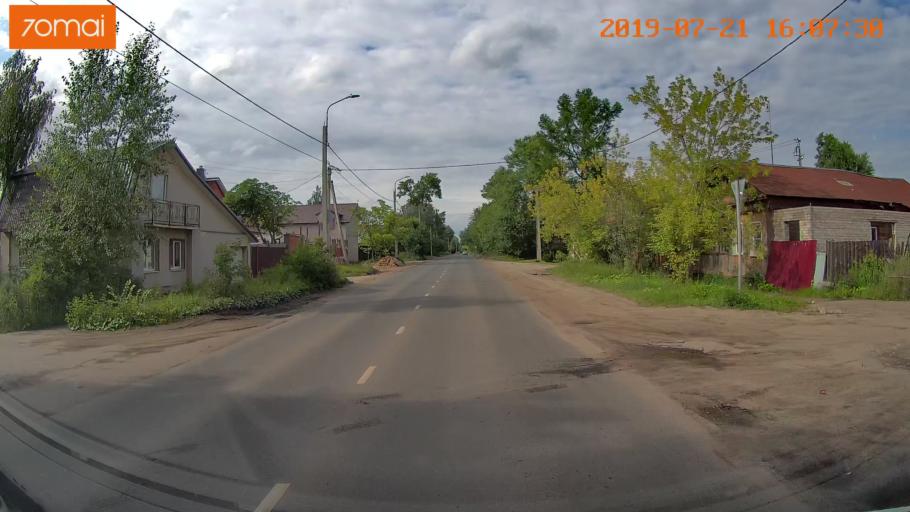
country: RU
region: Ivanovo
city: Bogorodskoye
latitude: 56.9916
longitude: 41.0312
